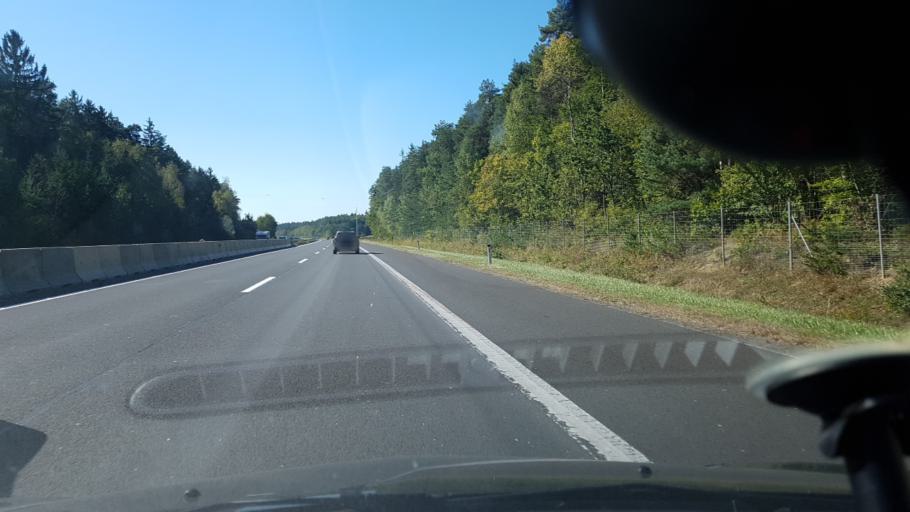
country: AT
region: Styria
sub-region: Politischer Bezirk Hartberg-Fuerstenfeld
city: Bad Waltersdorf
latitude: 47.1456
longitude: 15.9933
